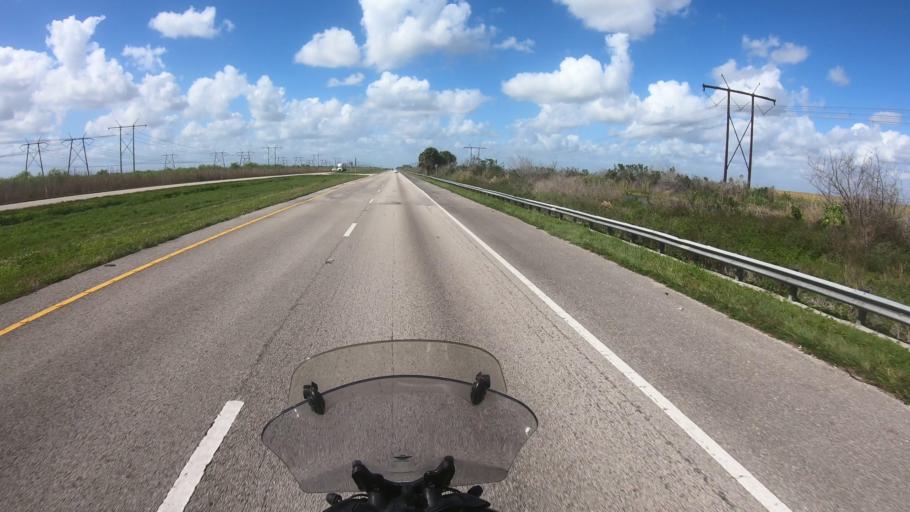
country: US
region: Florida
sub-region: Broward County
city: Weston
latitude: 26.2697
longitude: -80.4857
